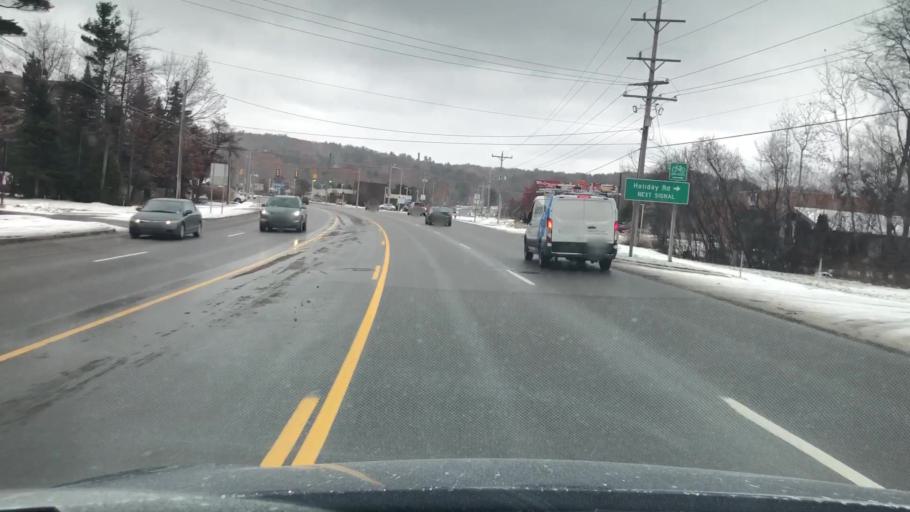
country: US
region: Michigan
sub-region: Grand Traverse County
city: Traverse City
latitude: 44.7462
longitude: -85.5308
